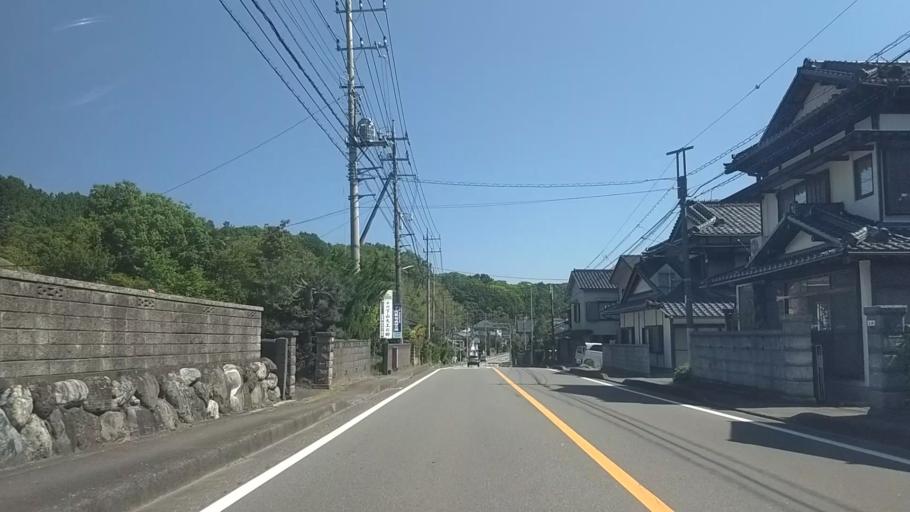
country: JP
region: Yamanashi
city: Ryuo
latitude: 35.4134
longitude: 138.4425
